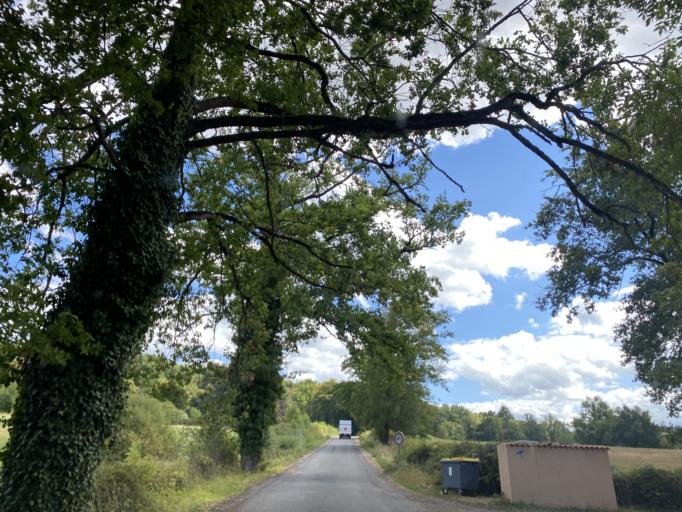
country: FR
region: Auvergne
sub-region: Departement du Puy-de-Dome
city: Courpiere
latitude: 45.7538
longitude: 3.5493
